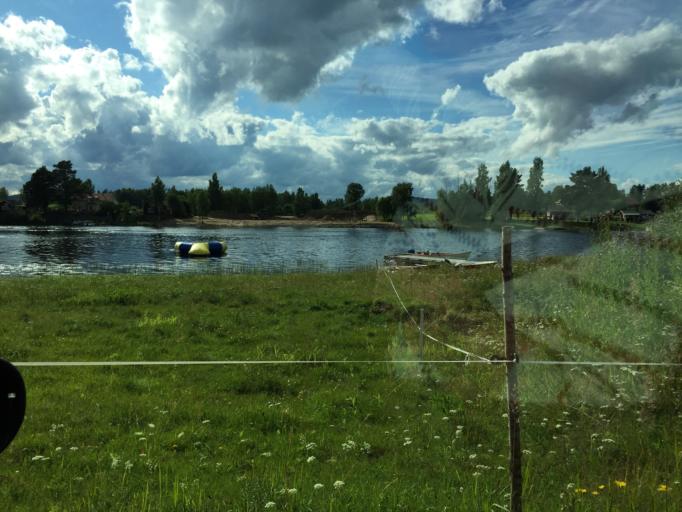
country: SE
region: Gaevleborg
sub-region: Ljusdals Kommun
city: Jaervsoe
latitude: 61.7622
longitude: 16.1698
